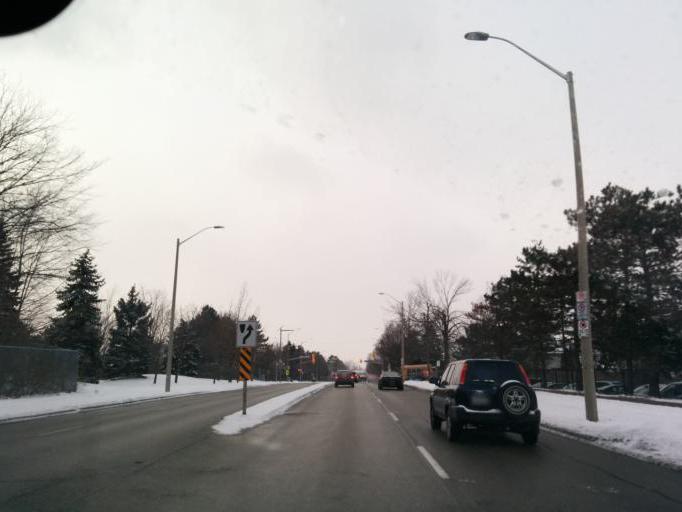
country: CA
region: Ontario
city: Mississauga
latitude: 43.5774
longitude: -79.7413
